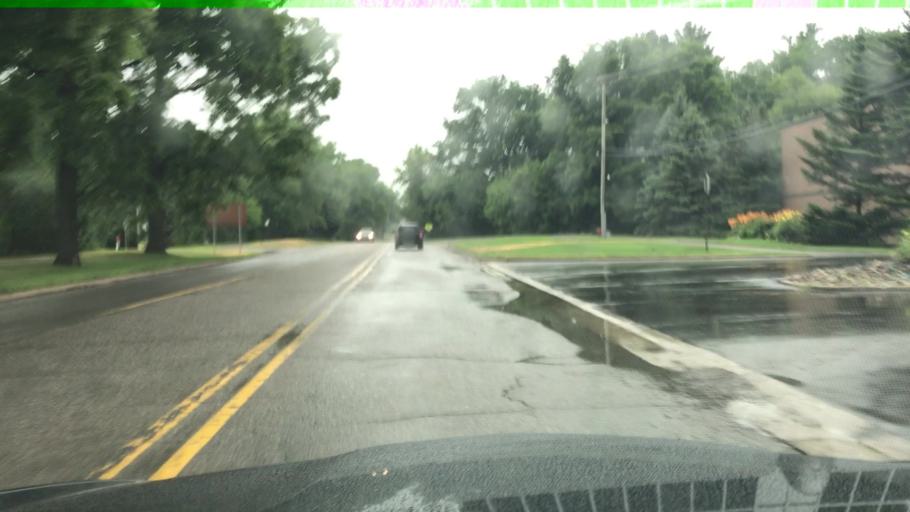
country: US
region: Michigan
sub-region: Oakland County
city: Lake Orion
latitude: 42.7362
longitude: -83.3057
